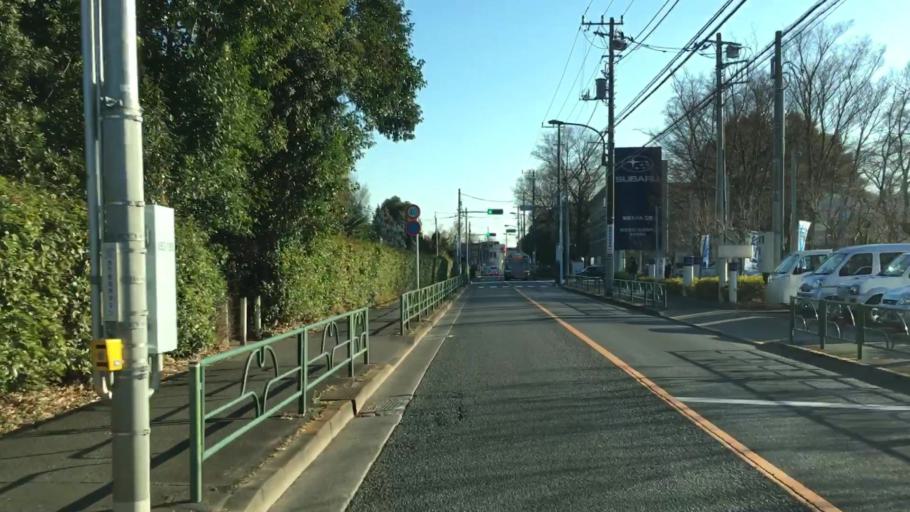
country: JP
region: Tokyo
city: Mitaka-shi
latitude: 35.6861
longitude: 139.5385
